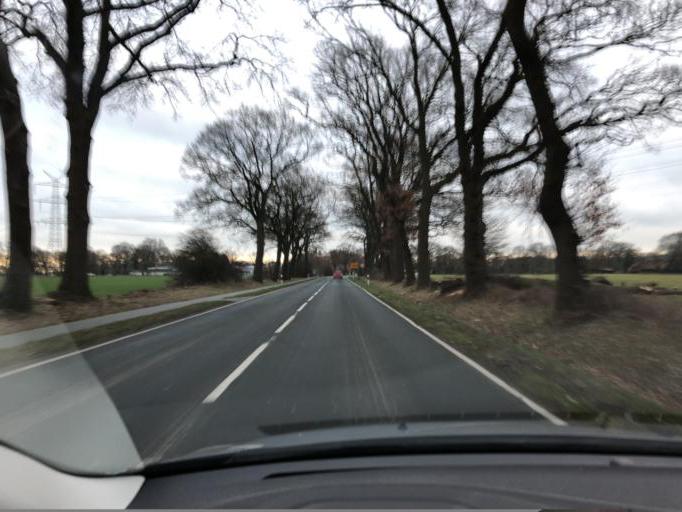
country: DE
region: Lower Saxony
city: Ganderkesee
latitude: 53.0672
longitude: 8.5704
